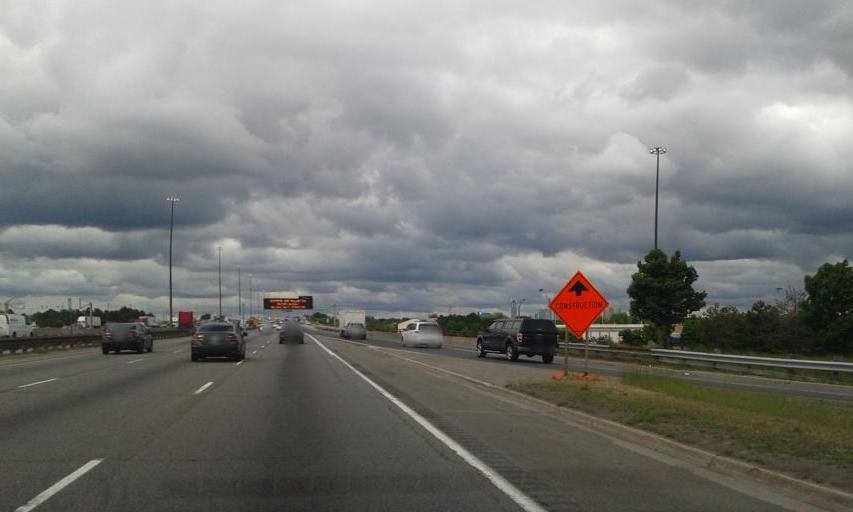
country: CA
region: Ontario
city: Scarborough
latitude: 43.7756
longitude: -79.2834
